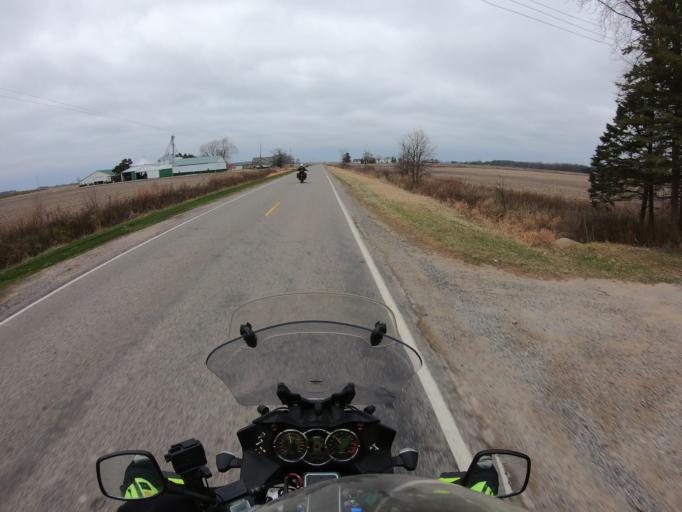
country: US
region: Michigan
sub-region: Saginaw County
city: Burt
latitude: 43.2438
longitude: -83.9864
